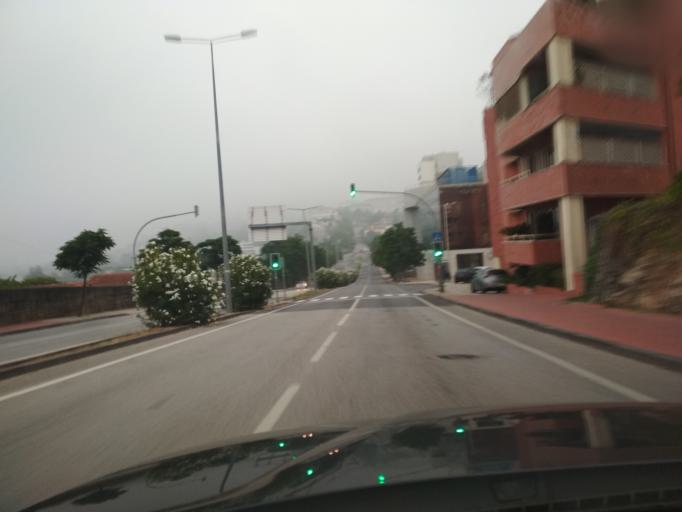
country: PT
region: Coimbra
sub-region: Coimbra
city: Coimbra
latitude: 40.1944
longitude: -8.4208
